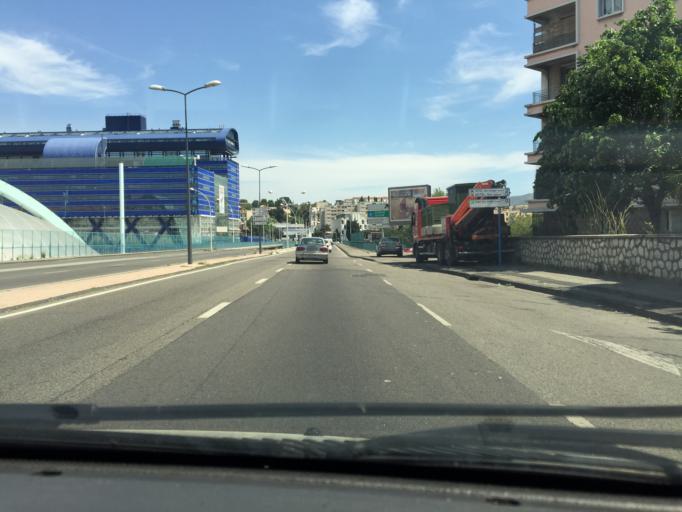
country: FR
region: Provence-Alpes-Cote d'Azur
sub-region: Departement des Bouches-du-Rhone
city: Marseille 13
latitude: 43.3152
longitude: 5.4026
